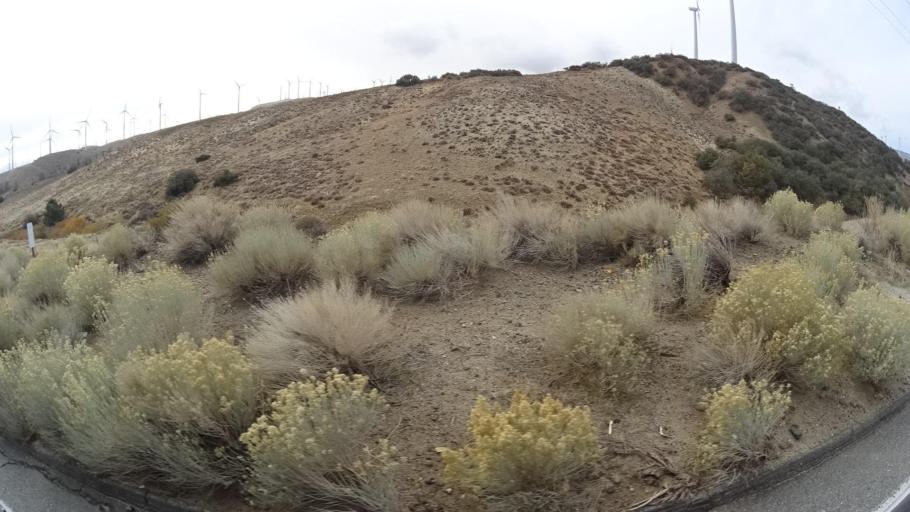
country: US
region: California
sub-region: Kern County
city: Tehachapi
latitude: 35.0549
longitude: -118.3667
